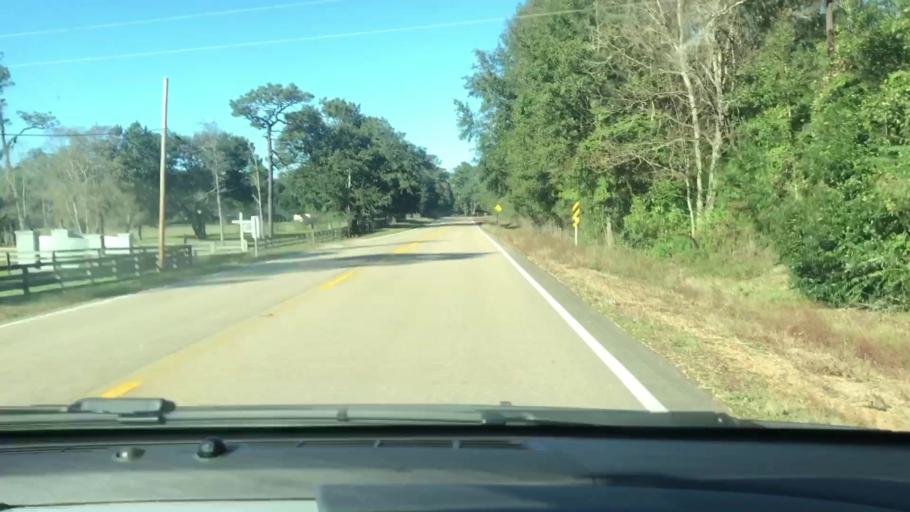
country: US
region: Louisiana
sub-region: Saint Tammany Parish
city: Abita Springs
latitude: 30.5453
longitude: -90.0453
